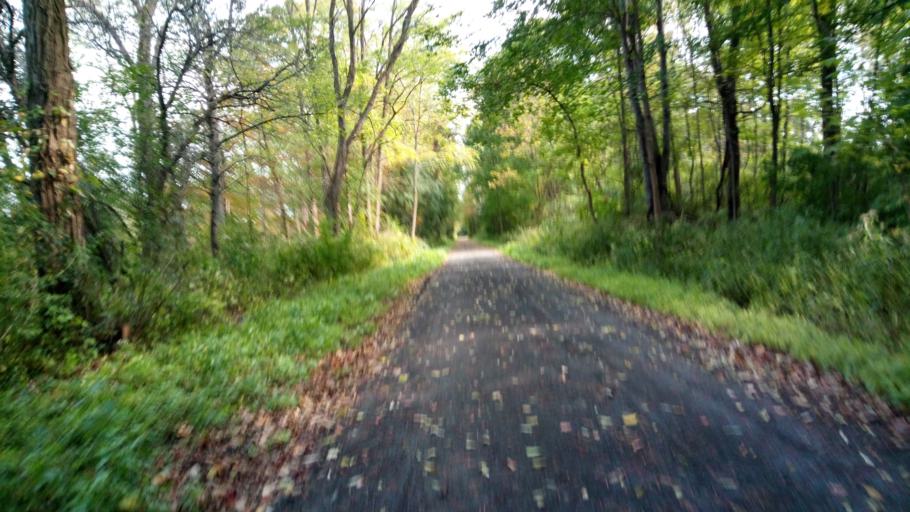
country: US
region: New York
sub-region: Wayne County
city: Clyde
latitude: 43.0677
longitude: -76.8531
